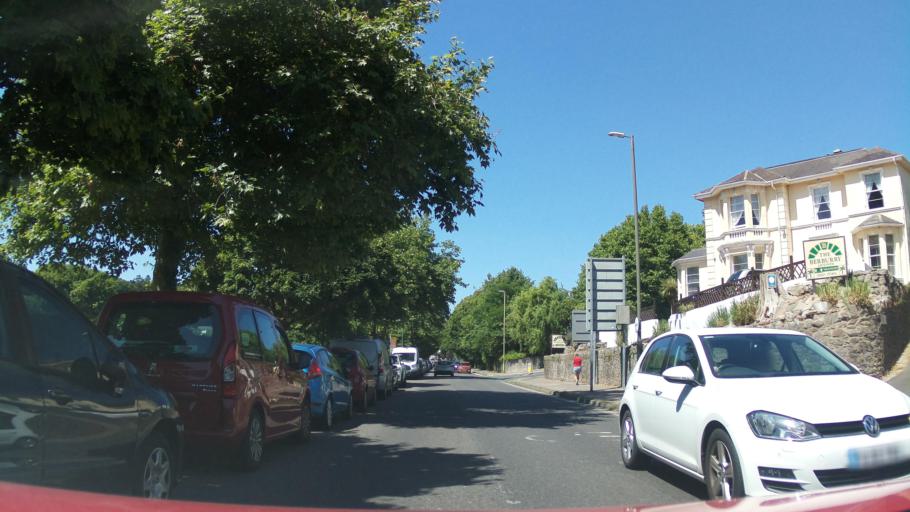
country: GB
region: England
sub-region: Borough of Torbay
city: Torquay
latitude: 50.4654
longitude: -3.5425
